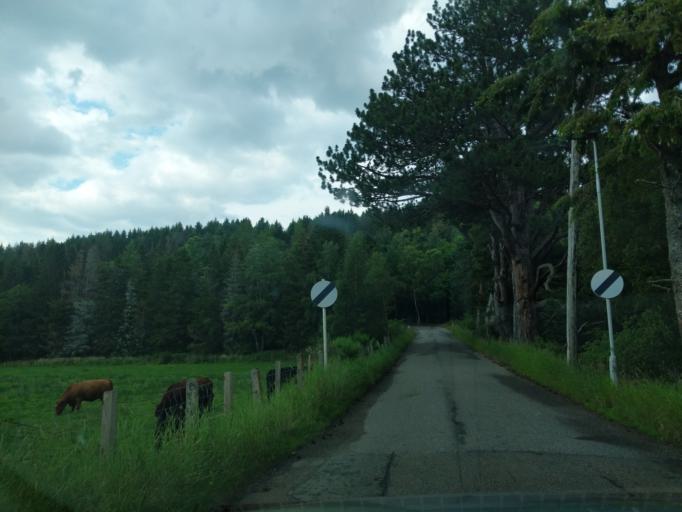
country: GB
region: Scotland
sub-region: Moray
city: Rothes
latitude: 57.4572
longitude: -3.3002
